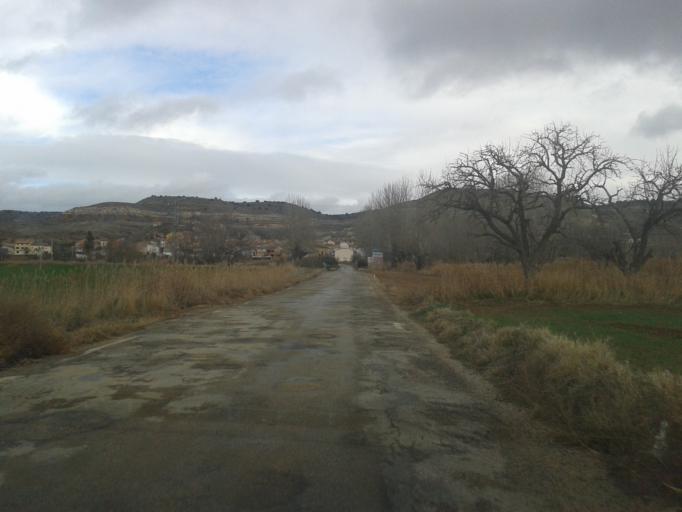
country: ES
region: Aragon
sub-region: Provincia de Teruel
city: Calamocha
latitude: 40.9278
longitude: -1.2618
